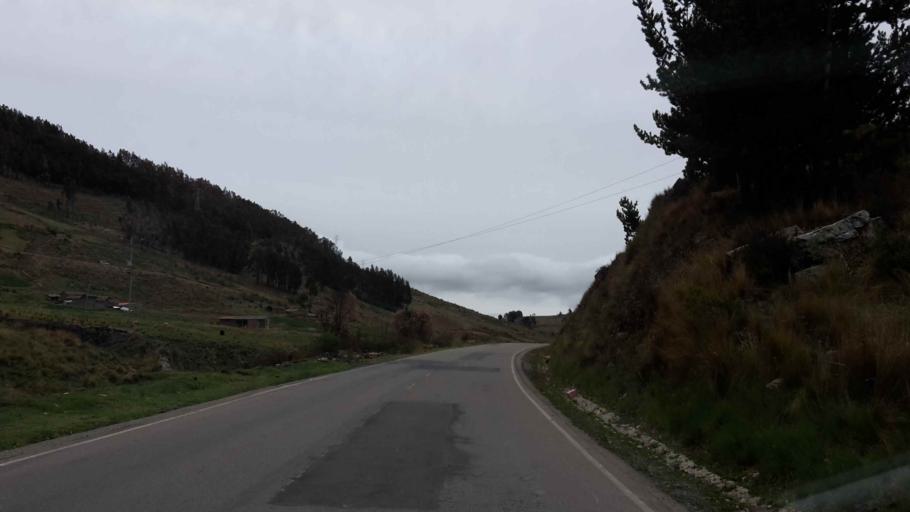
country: BO
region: Cochabamba
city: Arani
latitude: -17.4813
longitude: -65.5867
